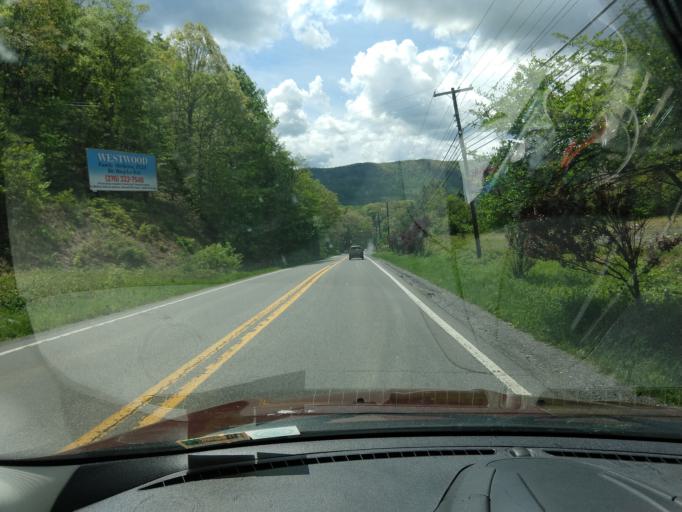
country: US
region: West Virginia
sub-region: Mercer County
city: Bluefield
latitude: 37.2593
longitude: -81.2345
